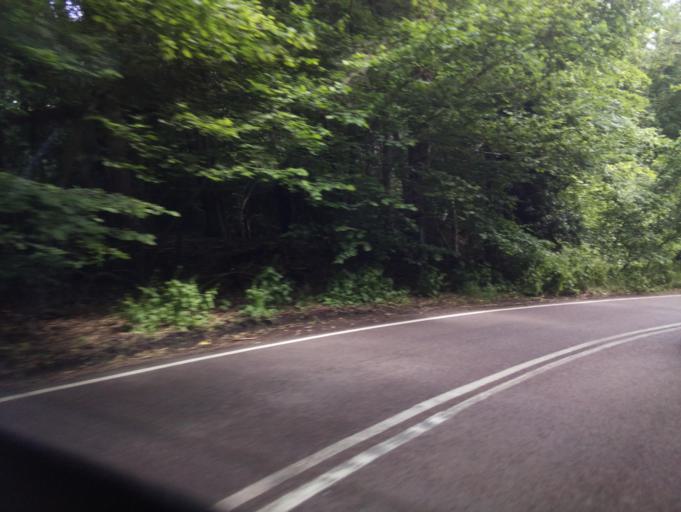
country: GB
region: England
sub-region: Hertfordshire
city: Kings Langley
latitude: 51.6748
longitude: -0.4509
